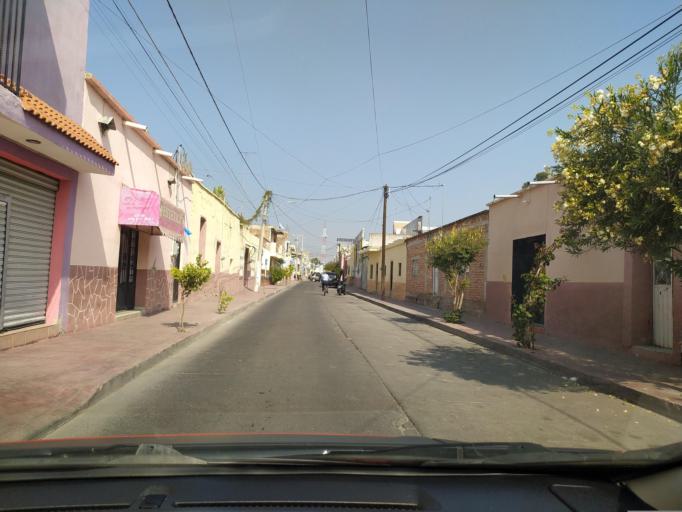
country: MX
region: Guanajuato
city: San Francisco del Rincon
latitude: 21.0278
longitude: -101.8796
